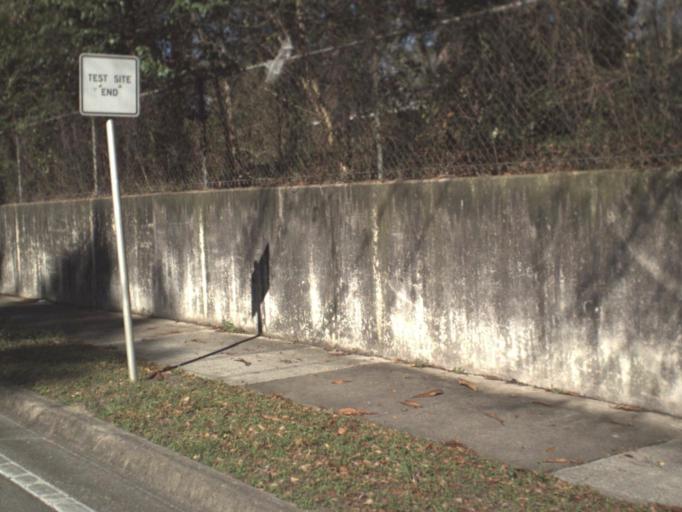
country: US
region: Florida
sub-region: Leon County
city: Tallahassee
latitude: 30.4530
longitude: -84.2625
